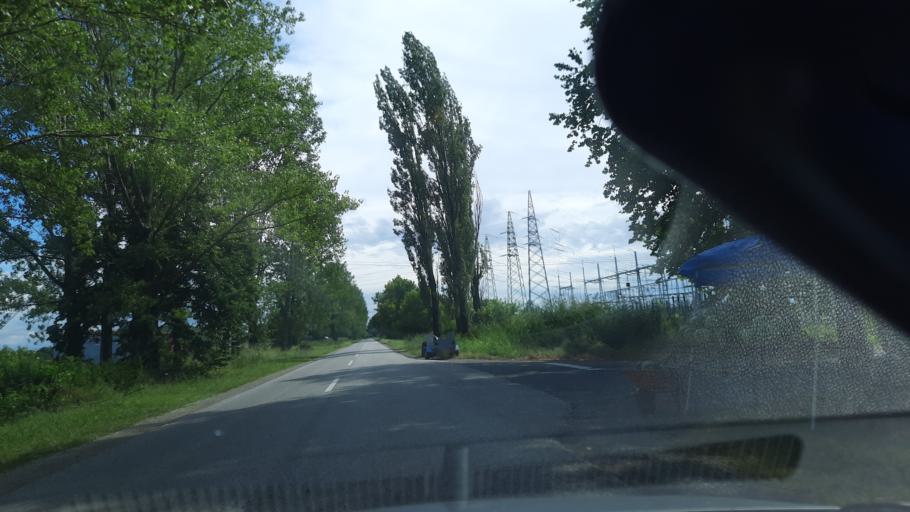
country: RS
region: Autonomna Pokrajina Vojvodina
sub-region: Sremski Okrug
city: Sremska Mitrovica
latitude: 45.0167
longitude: 19.6144
